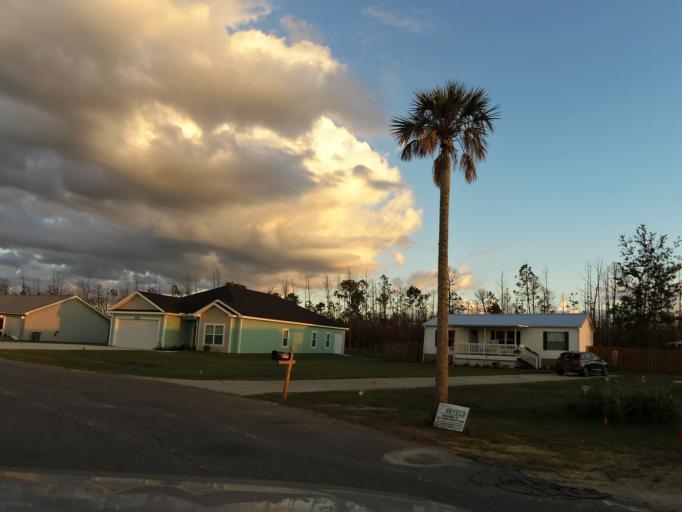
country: US
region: Florida
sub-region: Bay County
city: Mexico Beach
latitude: 29.9399
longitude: -85.3911
